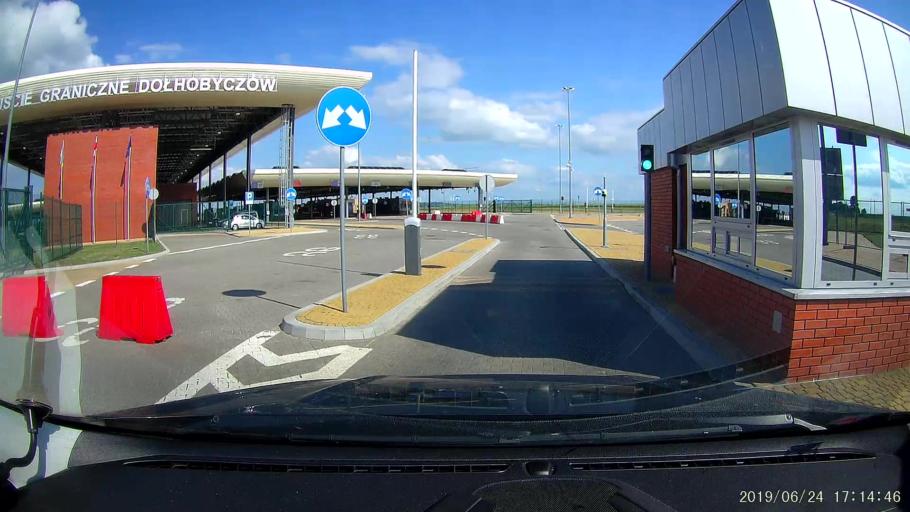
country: PL
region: Lublin Voivodeship
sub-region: Powiat hrubieszowski
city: Dolhobyczow
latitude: 50.5782
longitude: 24.0846
